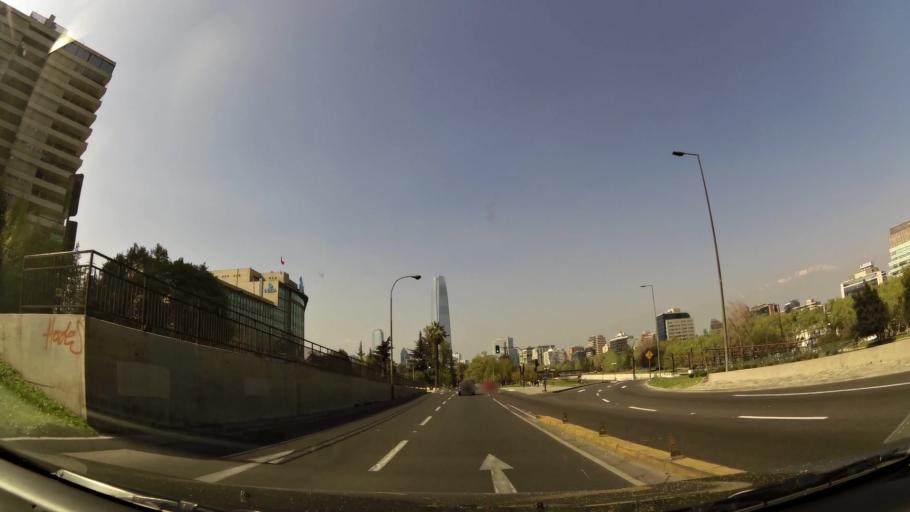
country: CL
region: Santiago Metropolitan
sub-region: Provincia de Santiago
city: Santiago
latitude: -33.4223
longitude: -70.6193
